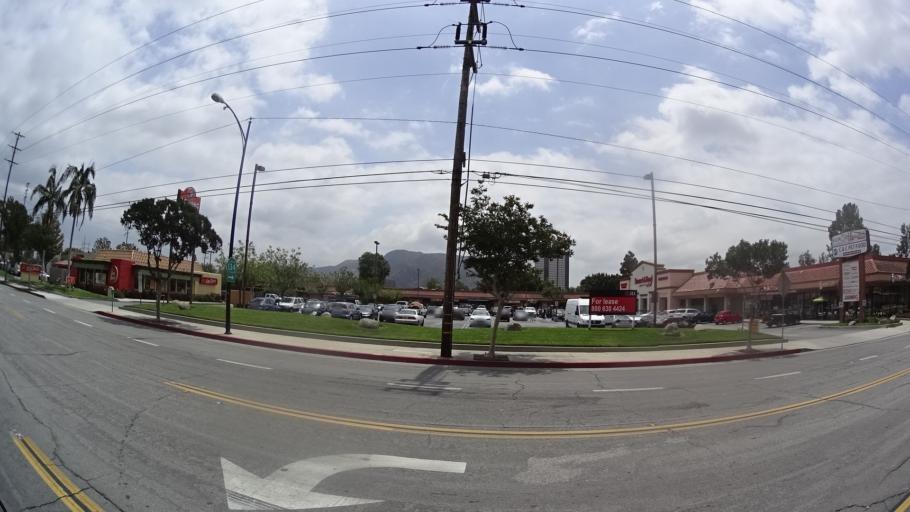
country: US
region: California
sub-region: Los Angeles County
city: Universal City
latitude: 34.1607
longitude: -118.3448
